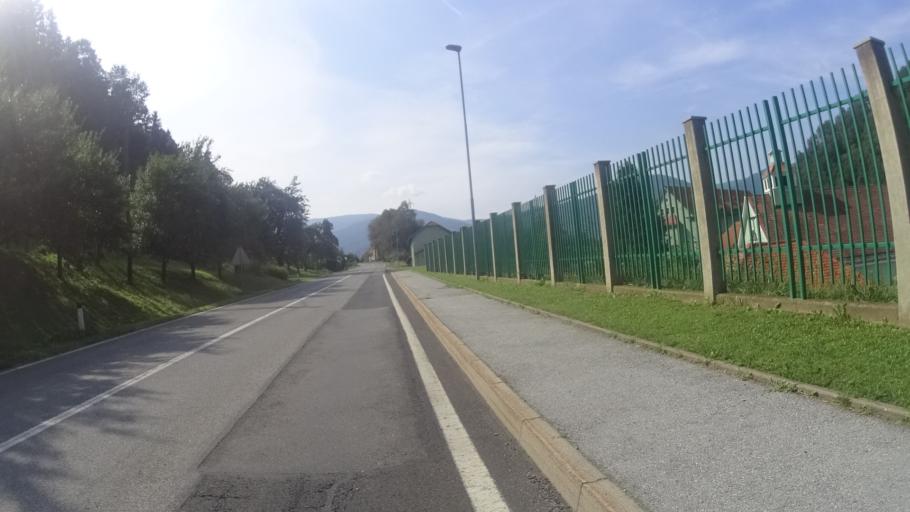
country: SI
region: Selnica ob Dravi
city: Selnica ob Dravi
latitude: 46.5588
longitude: 15.4581
